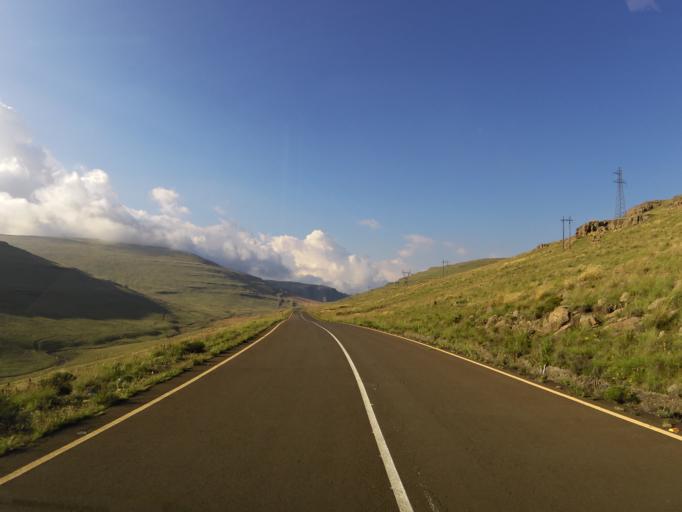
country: LS
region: Butha-Buthe
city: Butha-Buthe
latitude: -29.0942
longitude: 28.4243
